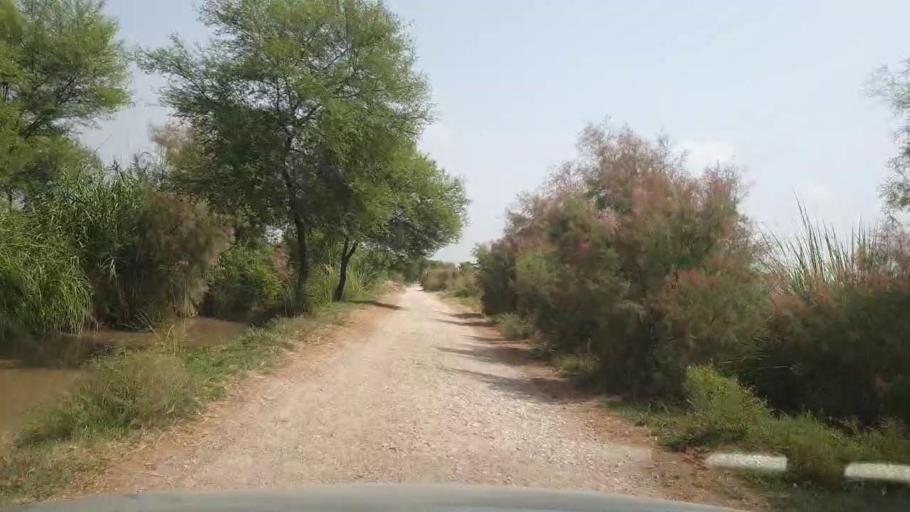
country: PK
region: Sindh
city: Garhi Yasin
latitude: 27.9352
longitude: 68.3663
